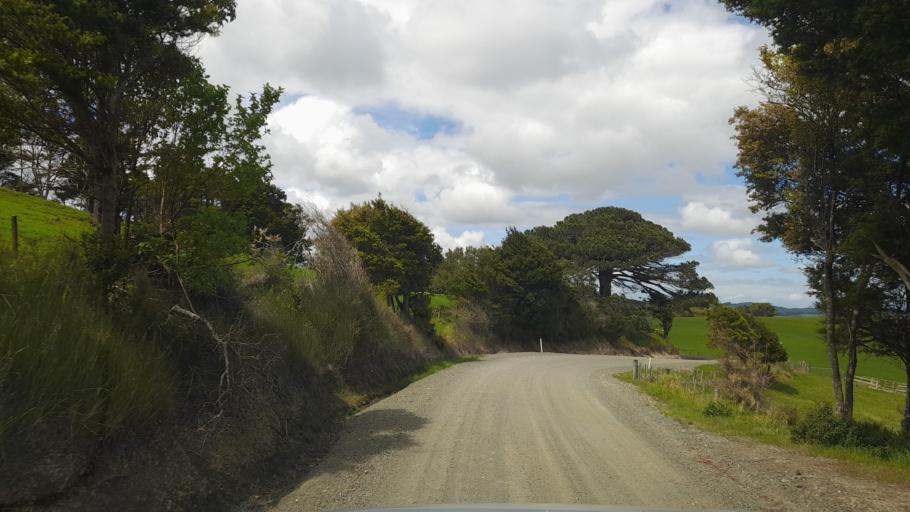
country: NZ
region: Auckland
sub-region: Auckland
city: Wellsford
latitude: -36.2158
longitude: 174.3201
